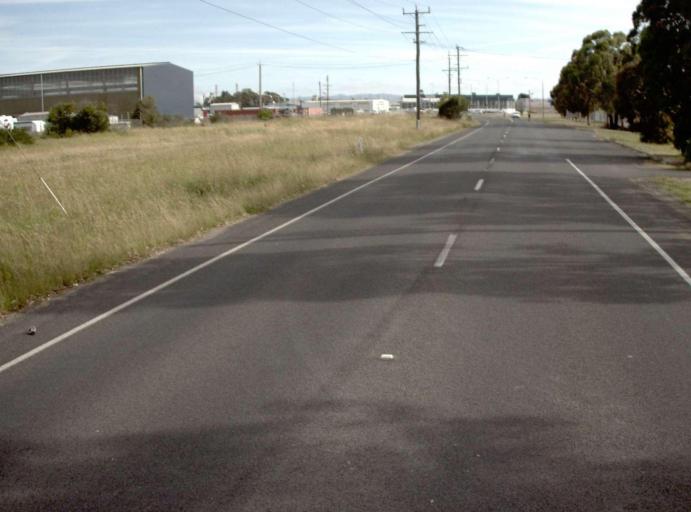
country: AU
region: Victoria
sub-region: Latrobe
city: Traralgon
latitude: -38.1875
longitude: 146.5612
